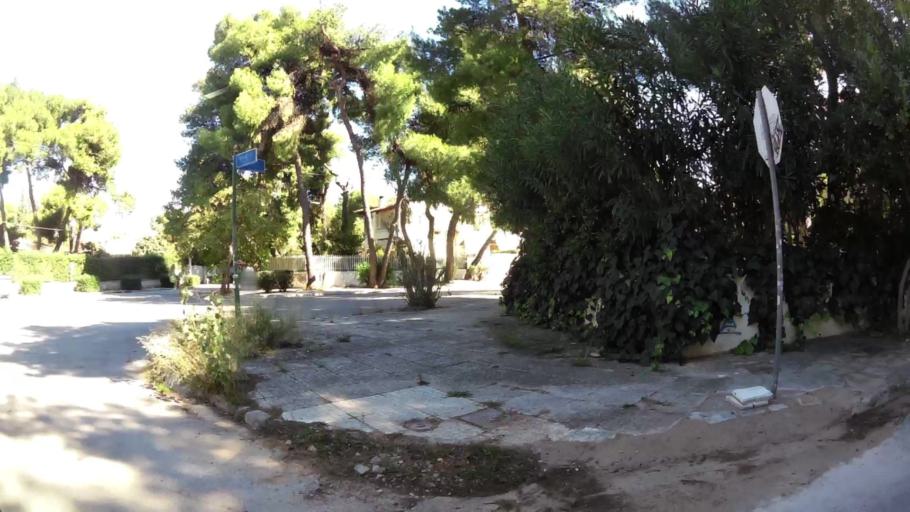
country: GR
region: Attica
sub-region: Nomarchia Athinas
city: Nea Erythraia
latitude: 38.0939
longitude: 23.7988
